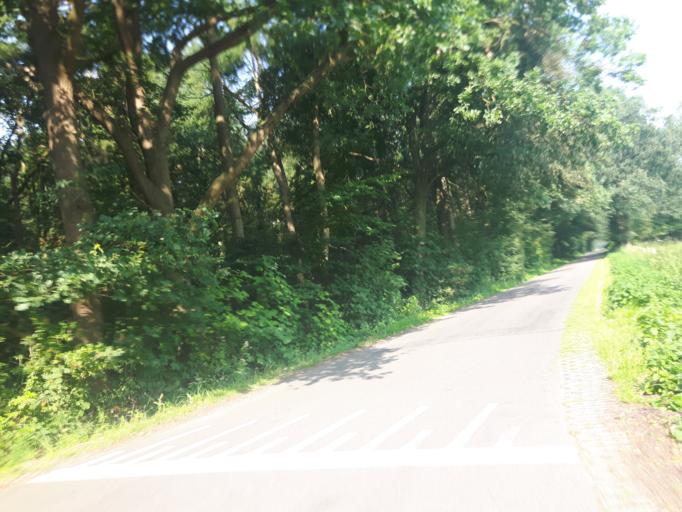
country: NL
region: Overijssel
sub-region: Gemeente Haaksbergen
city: Haaksbergen
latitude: 52.1873
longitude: 6.7781
